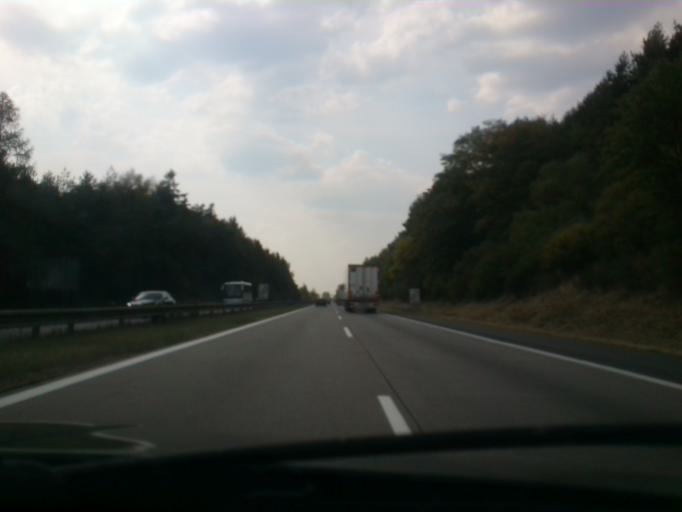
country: CZ
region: Central Bohemia
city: Divisov
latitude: 49.8354
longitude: 14.8451
